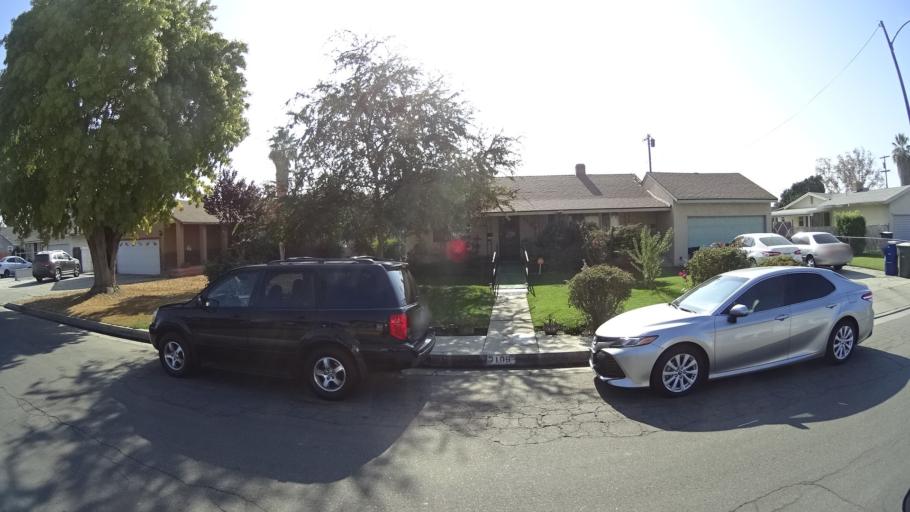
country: US
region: California
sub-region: Kern County
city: Bakersfield
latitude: 35.3502
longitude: -119.0373
